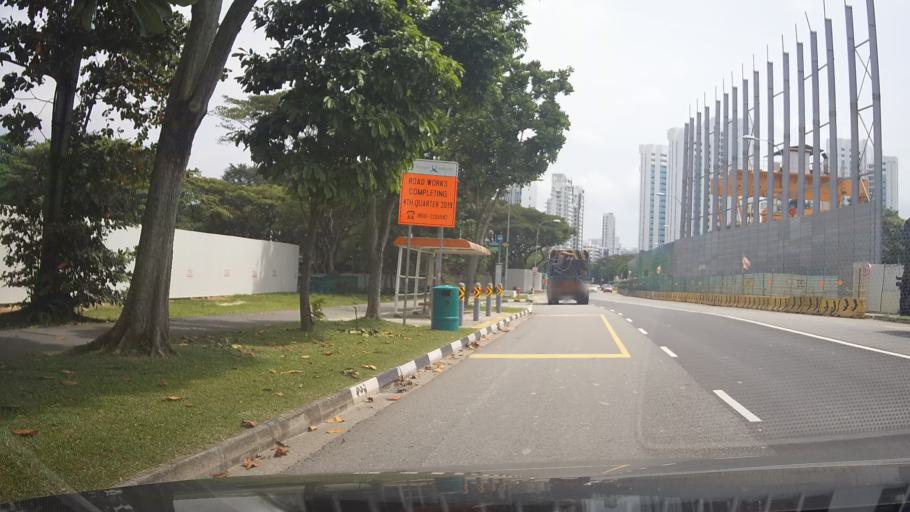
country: SG
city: Singapore
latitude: 1.2977
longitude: 103.8789
